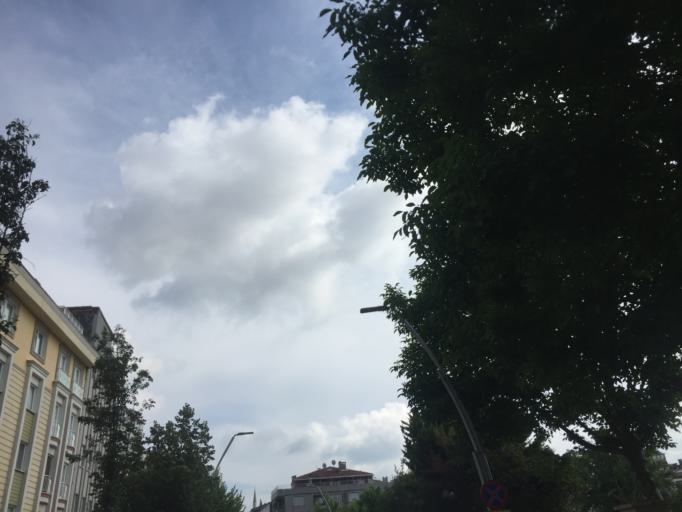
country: TR
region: Istanbul
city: Zeytinburnu
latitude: 41.0014
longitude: 28.9042
